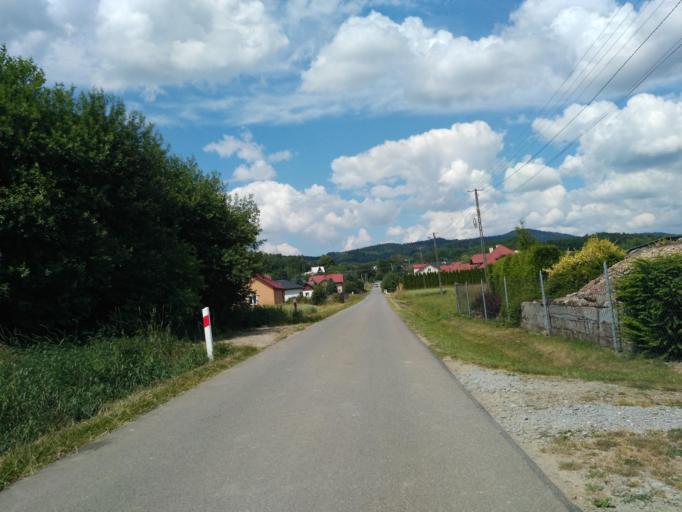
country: PL
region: Subcarpathian Voivodeship
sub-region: Powiat jasielski
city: Kolaczyce
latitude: 49.8043
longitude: 21.4109
